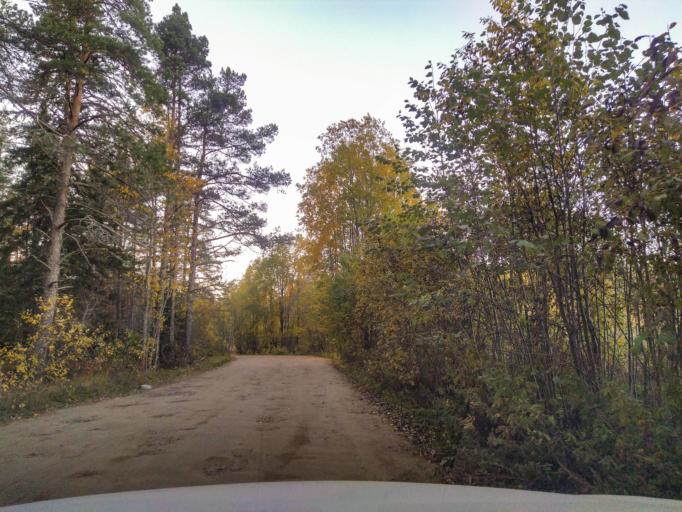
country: RU
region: Leningrad
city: Kuznechnoye
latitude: 61.2974
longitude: 30.0600
